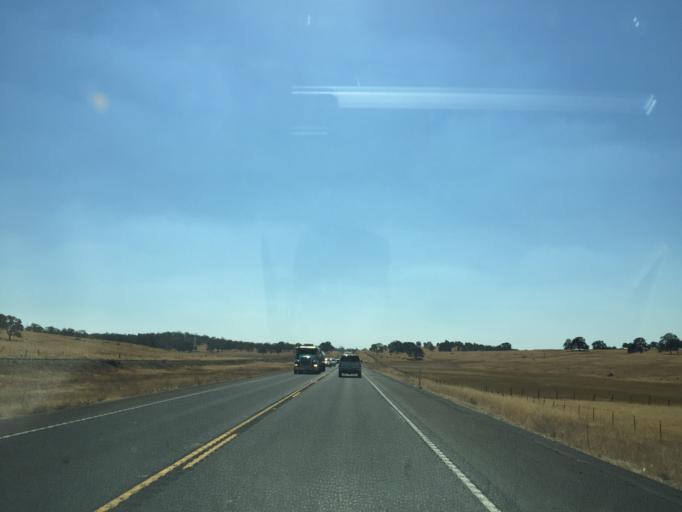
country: US
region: California
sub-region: Tuolumne County
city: Jamestown
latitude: 37.8564
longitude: -120.5113
